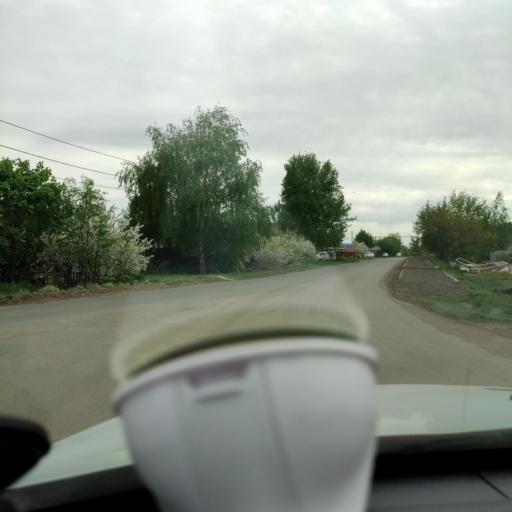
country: RU
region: Samara
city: Smyshlyayevka
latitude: 53.2220
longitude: 50.3377
